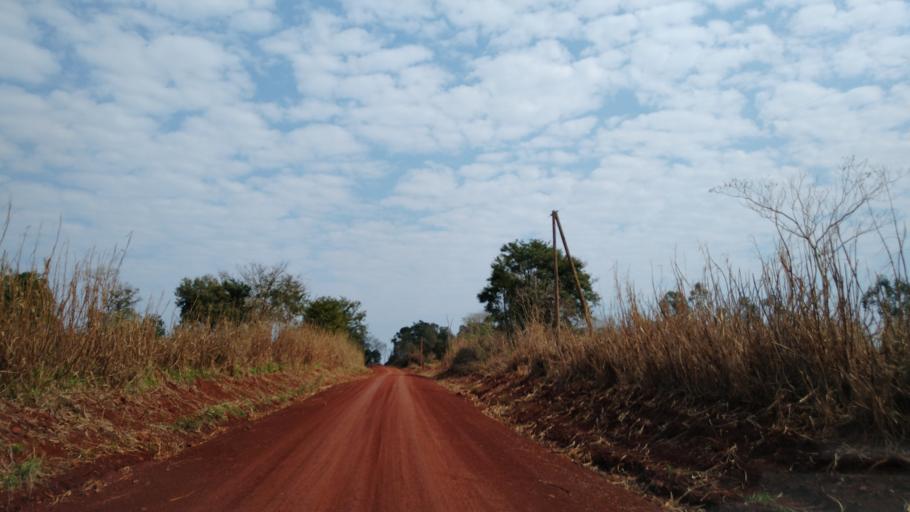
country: AR
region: Misiones
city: Capiovi
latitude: -26.9424
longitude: -55.0648
